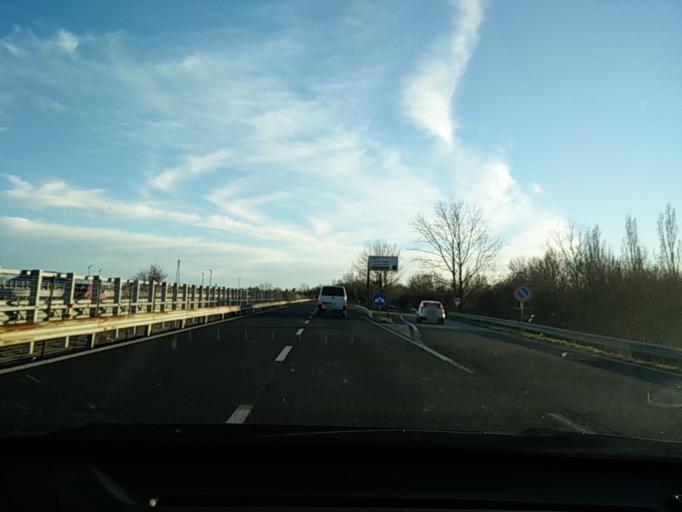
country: IT
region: Friuli Venezia Giulia
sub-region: Provincia di Udine
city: Colugna
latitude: 46.0872
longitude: 13.1929
